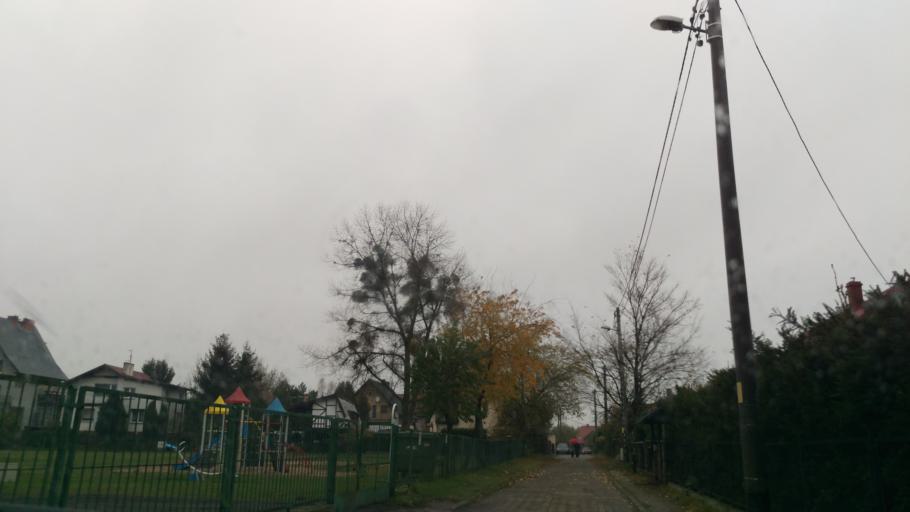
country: PL
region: West Pomeranian Voivodeship
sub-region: Szczecin
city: Szczecin
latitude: 53.4046
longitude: 14.6921
